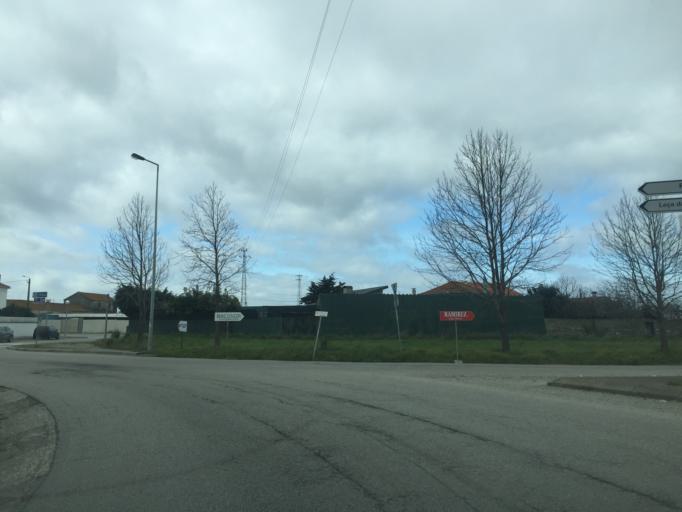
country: PT
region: Porto
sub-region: Matosinhos
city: Santa Cruz do Bispo
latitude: 41.2283
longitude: -8.6978
